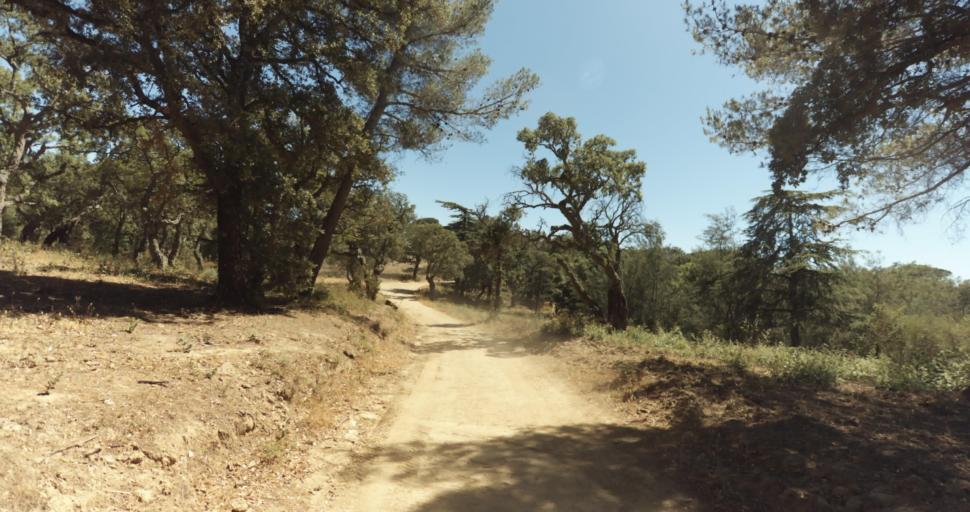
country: FR
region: Provence-Alpes-Cote d'Azur
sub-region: Departement du Var
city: Gassin
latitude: 43.2477
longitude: 6.5620
